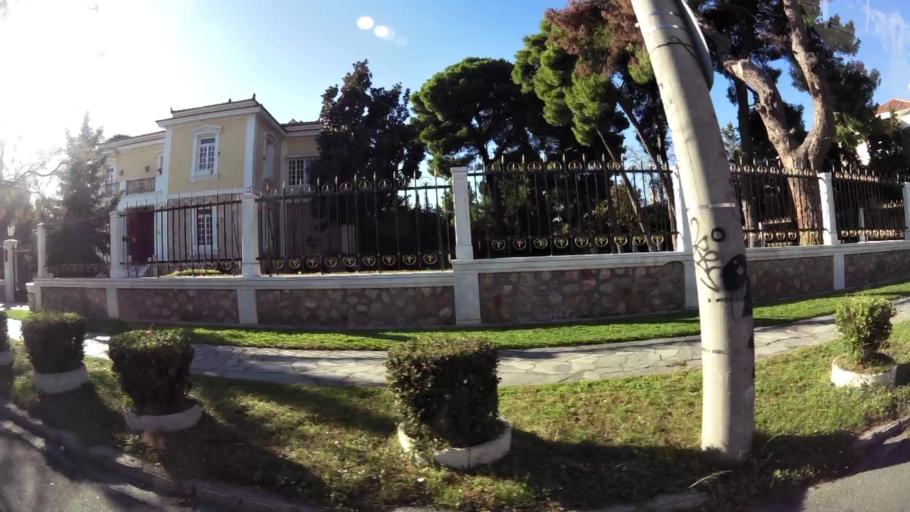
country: GR
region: Attica
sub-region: Nomarchia Athinas
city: Kifisia
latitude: 38.0787
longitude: 23.8137
